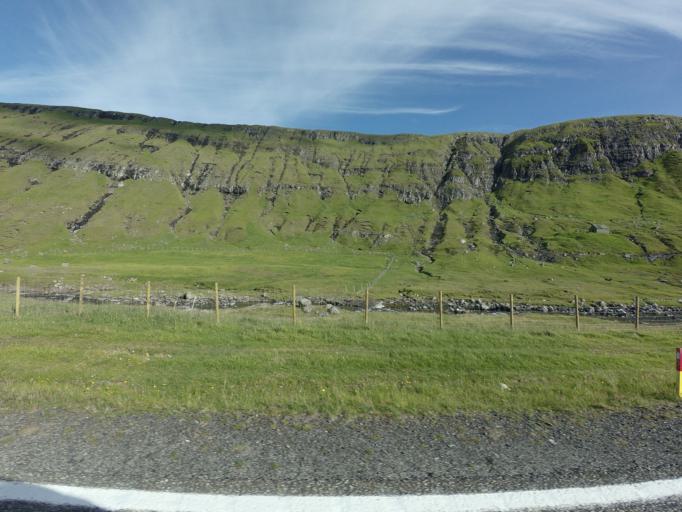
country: FO
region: Streymoy
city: Kollafjordhur
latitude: 62.1252
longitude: -7.0361
